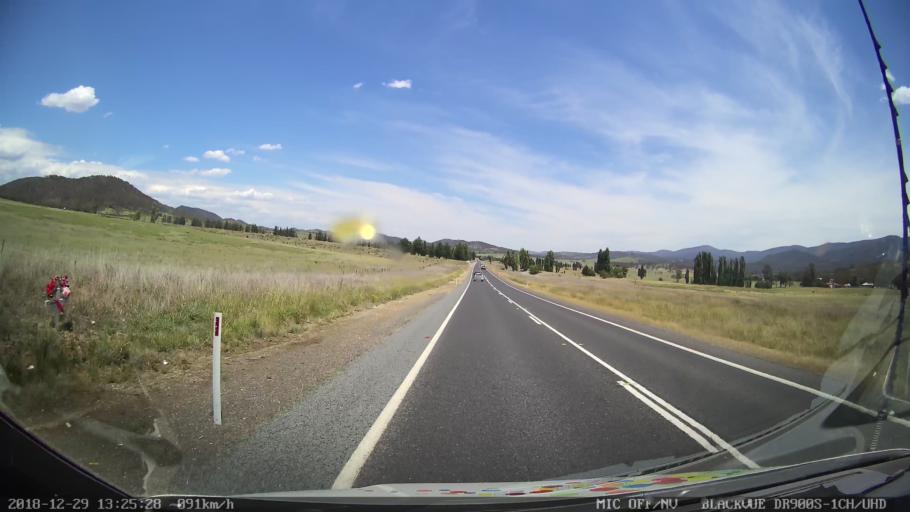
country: AU
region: New South Wales
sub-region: Cooma-Monaro
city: Cooma
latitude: -35.8427
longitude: 149.1614
